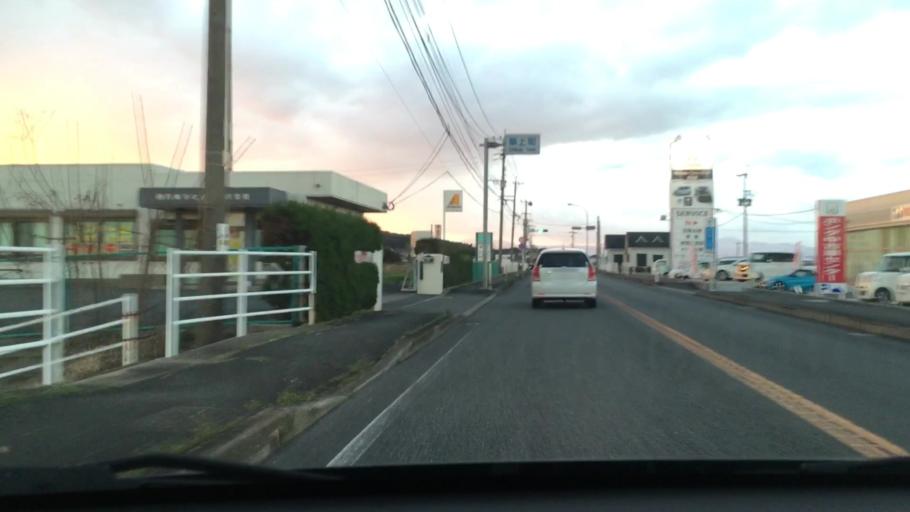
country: JP
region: Fukuoka
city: Shiida
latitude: 33.6297
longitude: 131.0851
